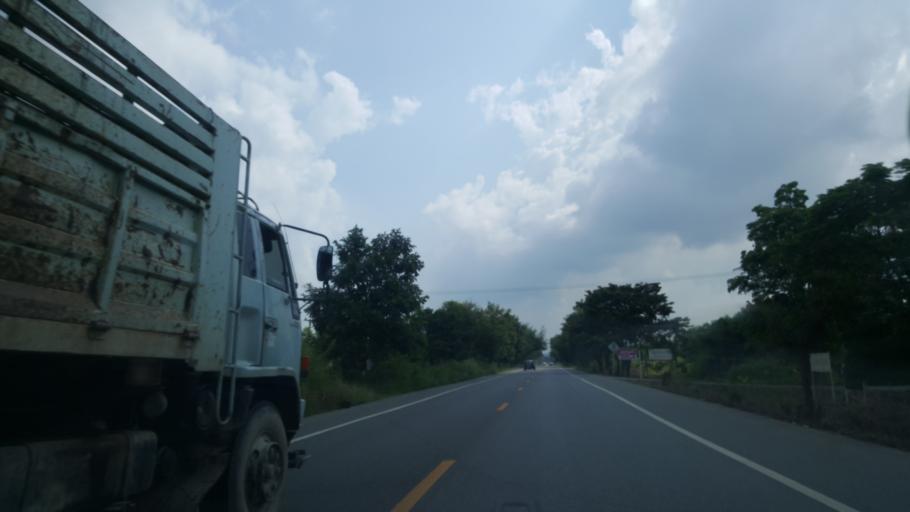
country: TH
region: Chon Buri
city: Sattahip
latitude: 12.7266
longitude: 100.9644
